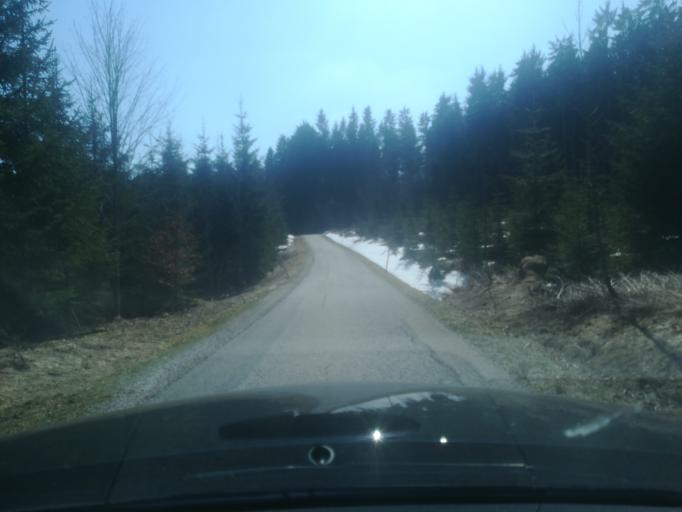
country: AT
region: Lower Austria
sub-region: Politischer Bezirk Zwettl
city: Langschlag
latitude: 48.5045
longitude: 14.8540
